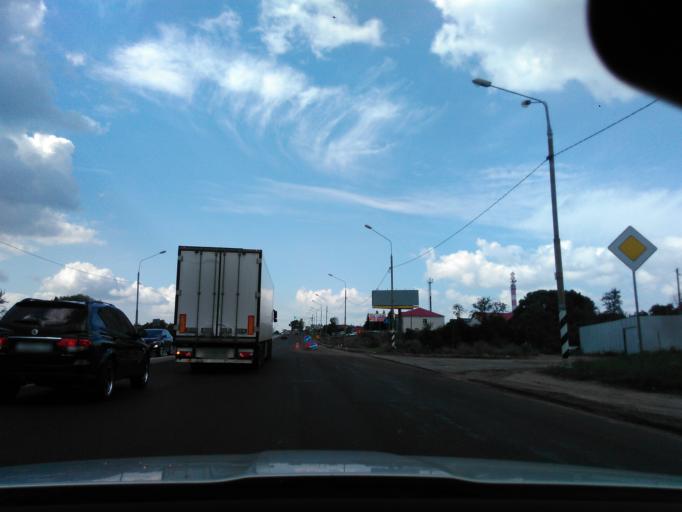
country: RU
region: Moskovskaya
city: Peshki
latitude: 56.1236
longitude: 37.0766
